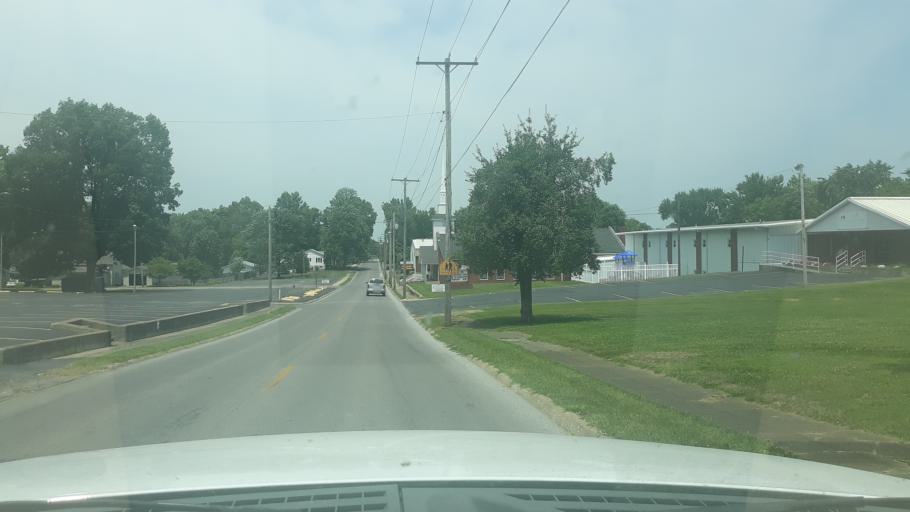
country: US
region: Illinois
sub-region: Saline County
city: Harrisburg
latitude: 37.7216
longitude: -88.5531
